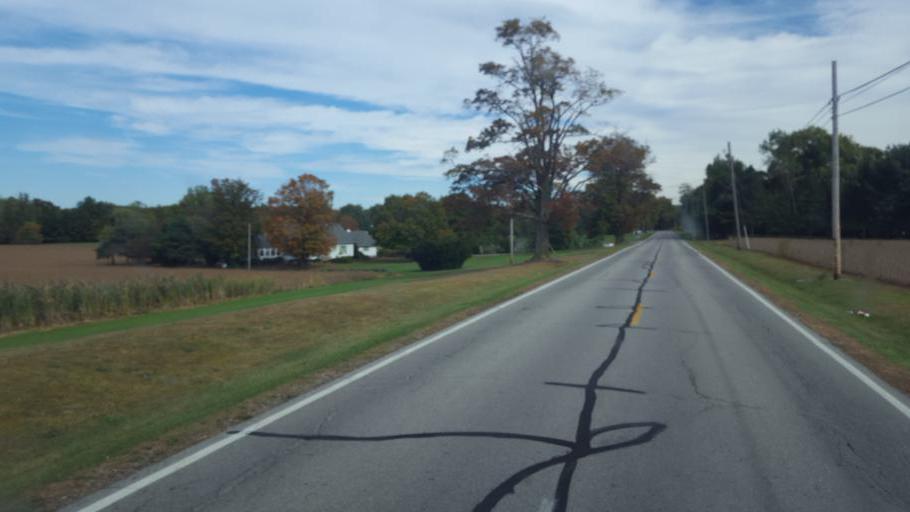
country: US
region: Ohio
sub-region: Lorain County
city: Vermilion-on-the-Lake
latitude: 41.3865
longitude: -82.3015
